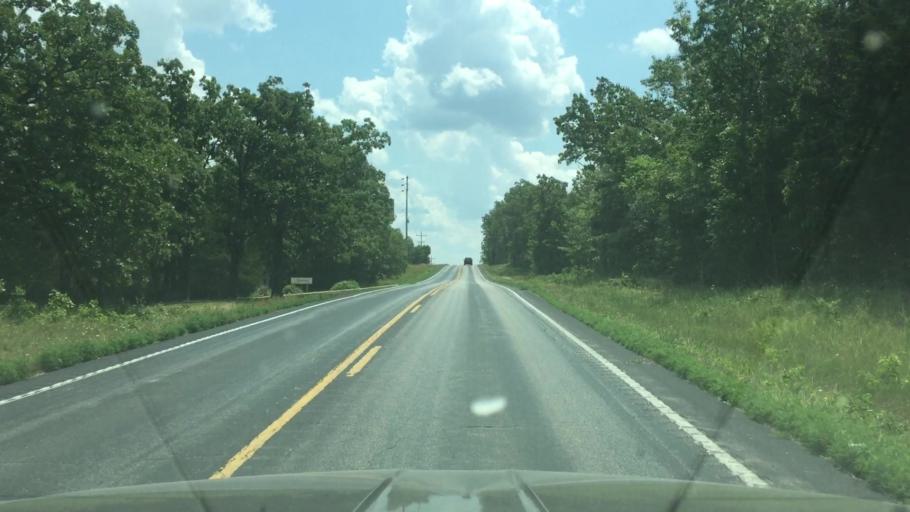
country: US
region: Missouri
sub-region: Camden County
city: Osage Beach
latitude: 38.1383
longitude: -92.5784
